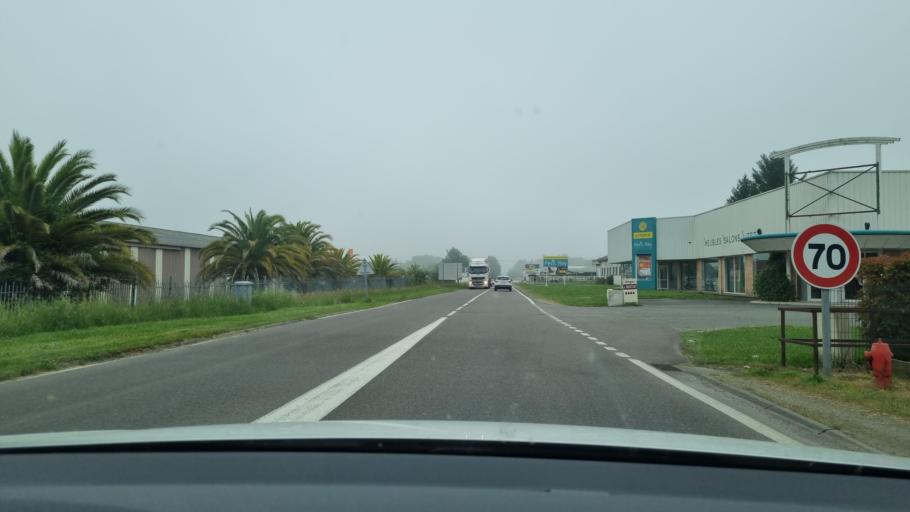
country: FR
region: Aquitaine
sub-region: Departement des Landes
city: Hagetmau
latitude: 43.6382
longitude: -0.6135
